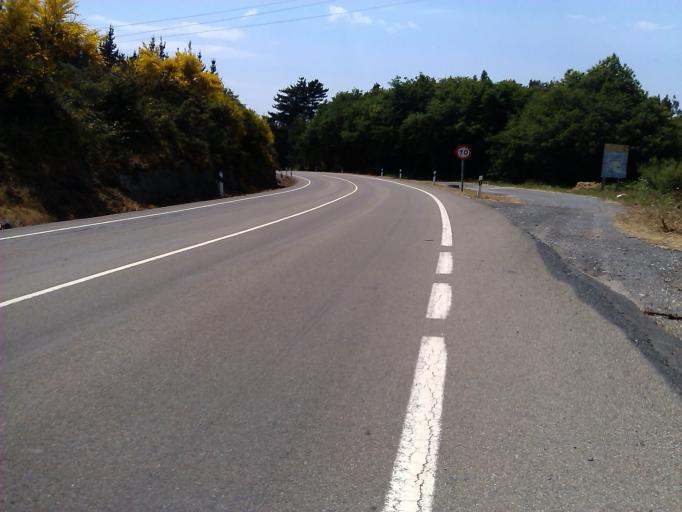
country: ES
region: Galicia
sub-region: Provincia de Lugo
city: Monterroso
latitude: 42.8754
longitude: -7.8527
